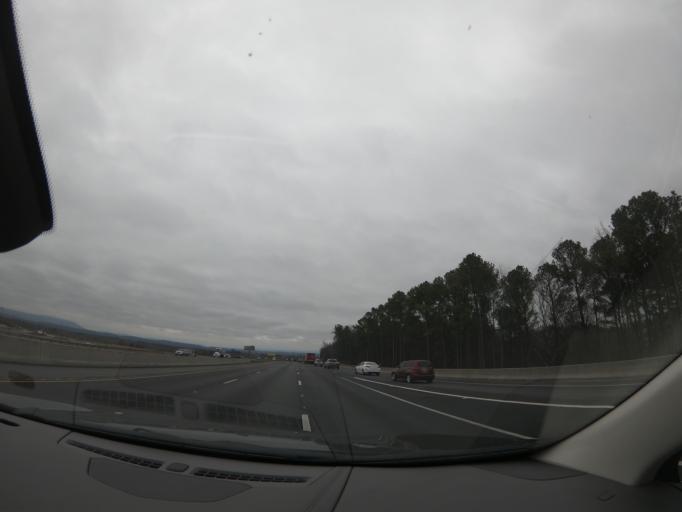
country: US
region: Georgia
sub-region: Catoosa County
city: Indian Springs
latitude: 34.9707
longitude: -85.1933
